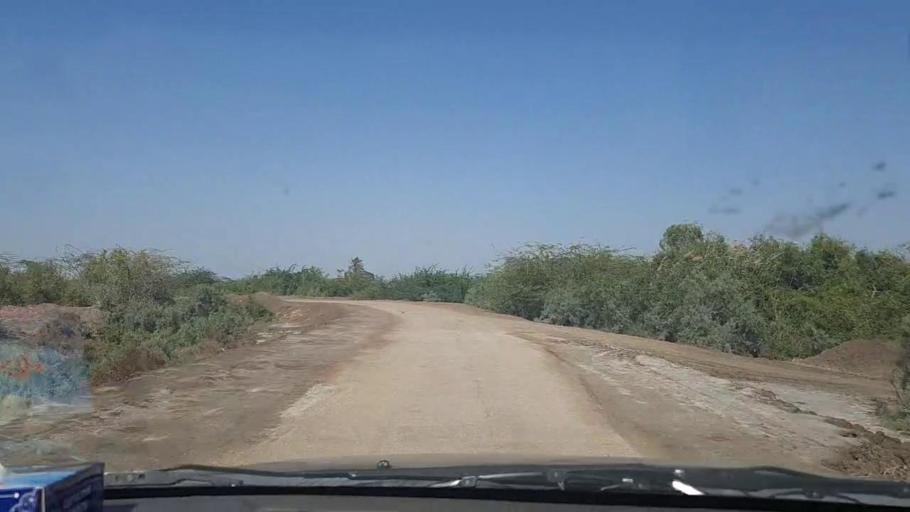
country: PK
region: Sindh
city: Chuhar Jamali
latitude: 24.2777
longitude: 67.7627
